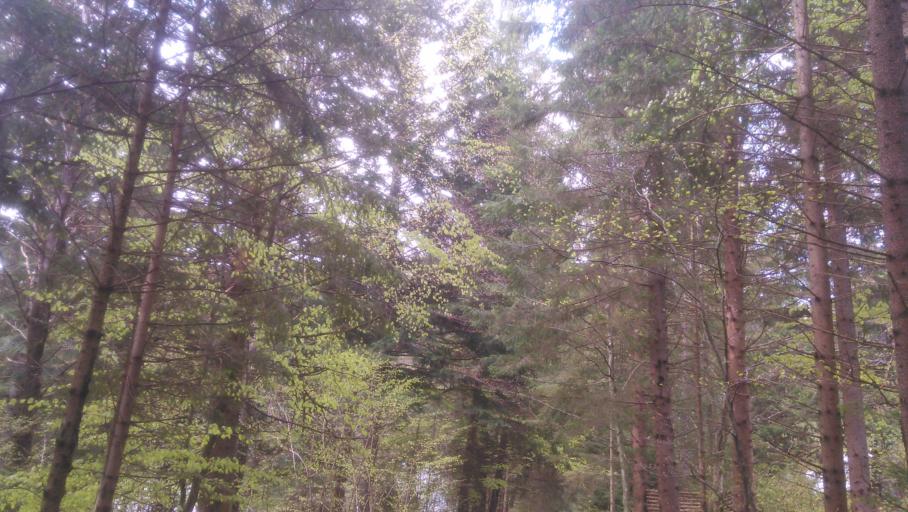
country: SK
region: Banskobystricky
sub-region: Okres Banska Bystrica
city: Brezno
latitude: 48.8758
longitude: 19.5693
